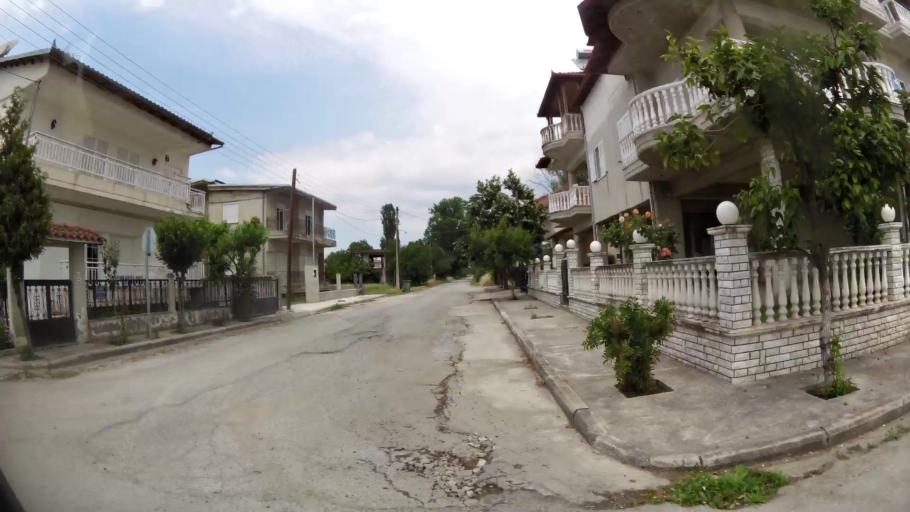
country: GR
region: Central Macedonia
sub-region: Nomos Pierias
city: Kallithea
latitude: 40.2737
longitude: 22.5709
